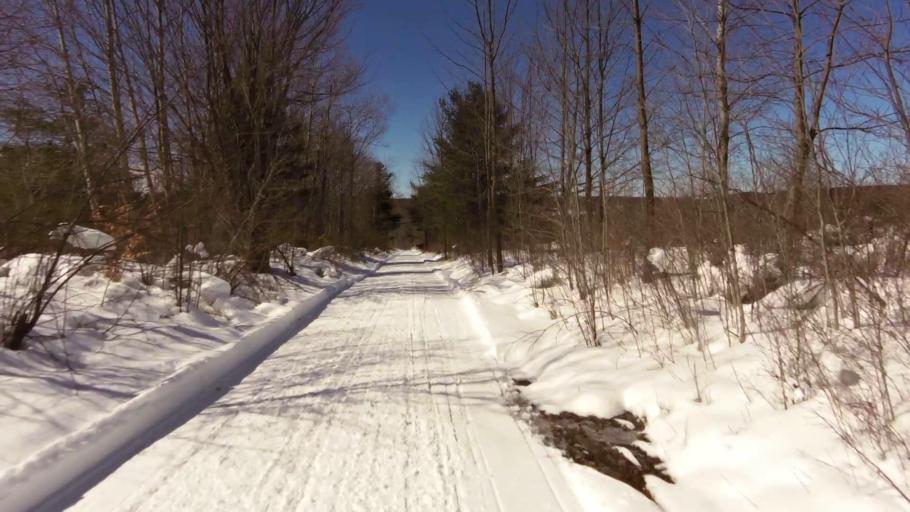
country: US
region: New York
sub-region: Allegany County
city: Cuba
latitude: 42.3267
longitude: -78.2439
